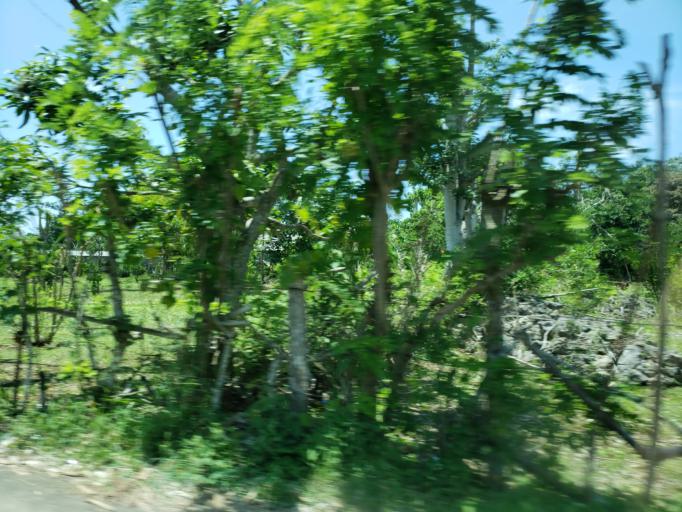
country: ID
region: Bali
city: Pecatu
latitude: -8.8382
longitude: 115.1253
